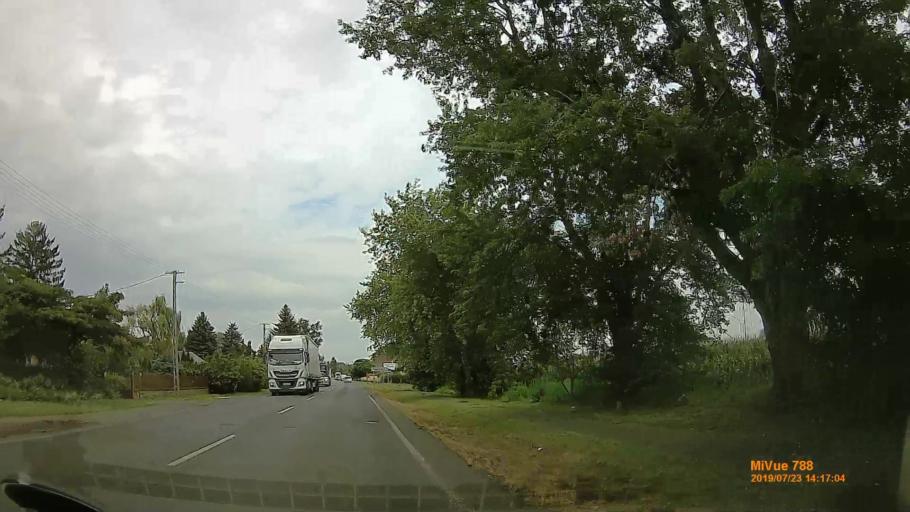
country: HU
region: Szabolcs-Szatmar-Bereg
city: Nagycserkesz
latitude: 47.9622
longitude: 21.5461
